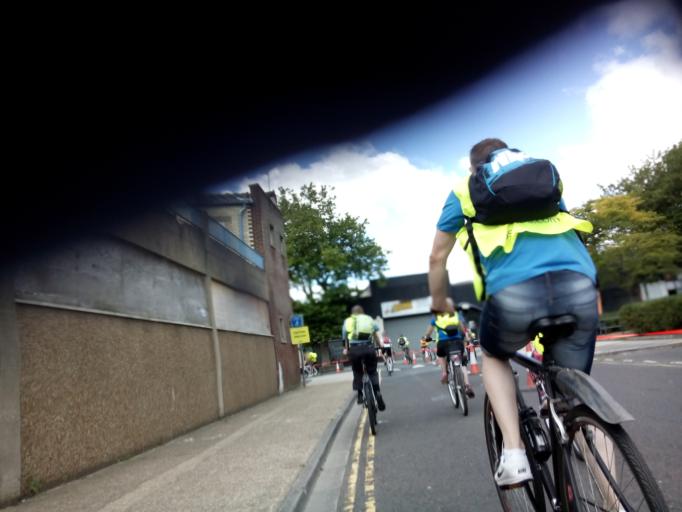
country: GB
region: England
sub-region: Suffolk
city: Ipswich
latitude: 52.0545
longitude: 1.1482
